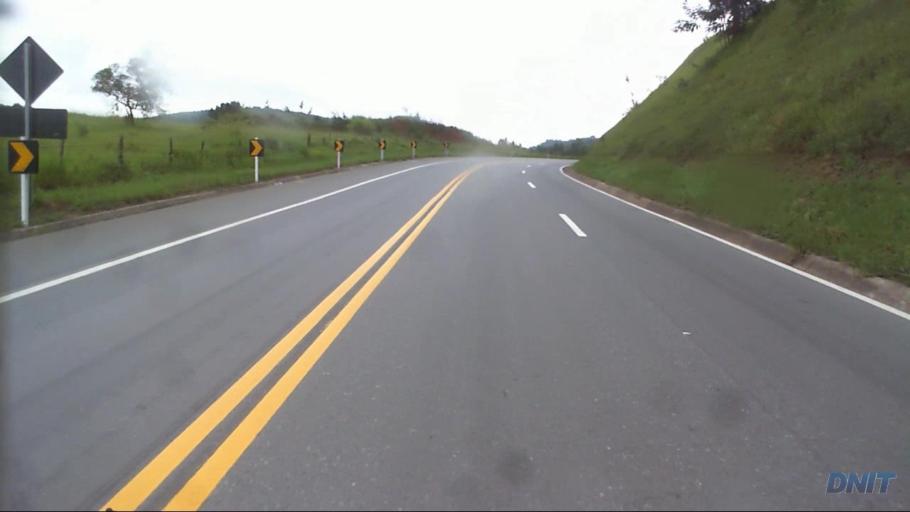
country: BR
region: Minas Gerais
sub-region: Nova Era
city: Nova Era
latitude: -19.7244
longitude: -43.0094
